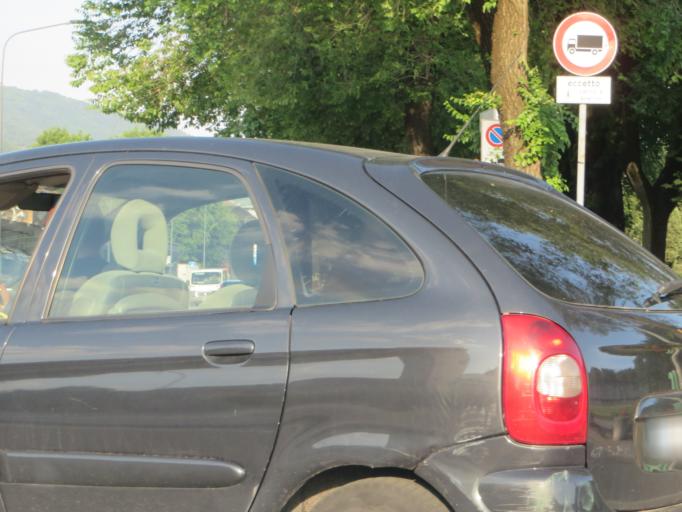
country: IT
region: Lombardy
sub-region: Provincia di Brescia
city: Brescia
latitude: 45.5439
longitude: 10.2010
